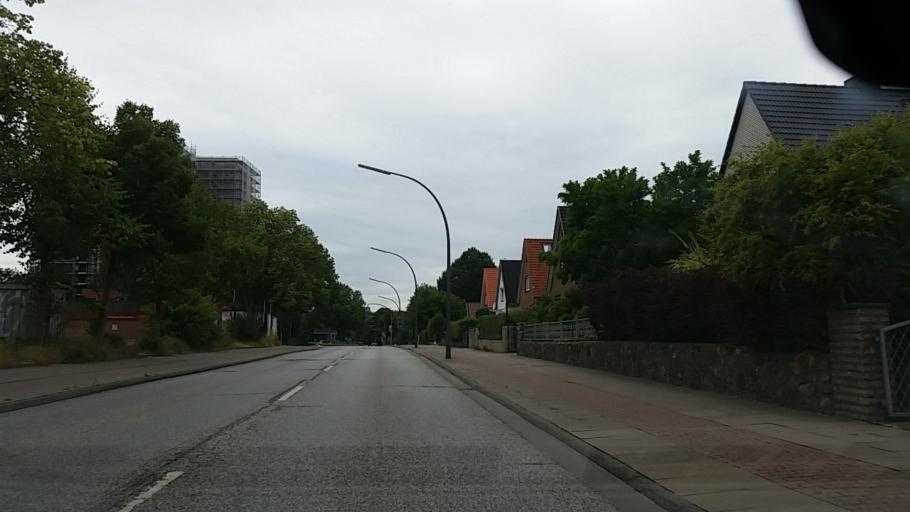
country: DE
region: Hamburg
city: Bergedorf
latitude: 53.5042
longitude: 10.2139
